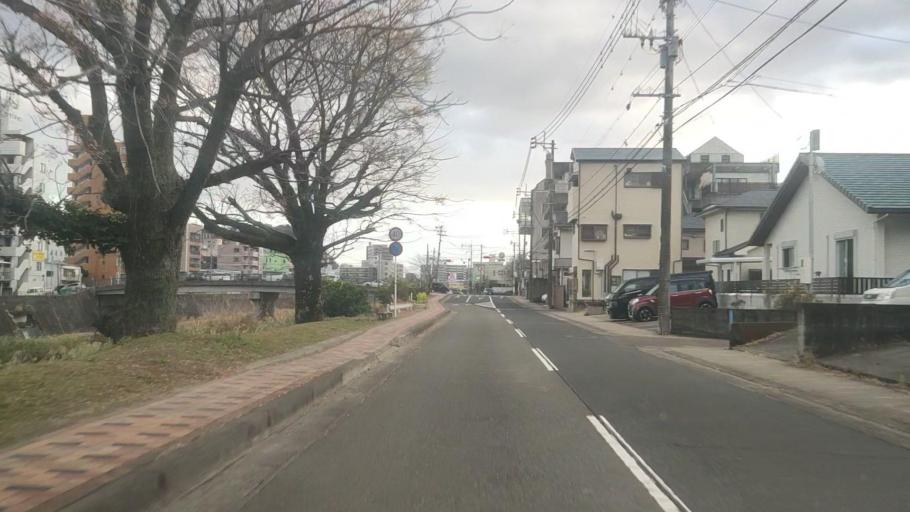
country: JP
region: Kagoshima
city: Kagoshima-shi
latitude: 31.6061
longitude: 130.5358
